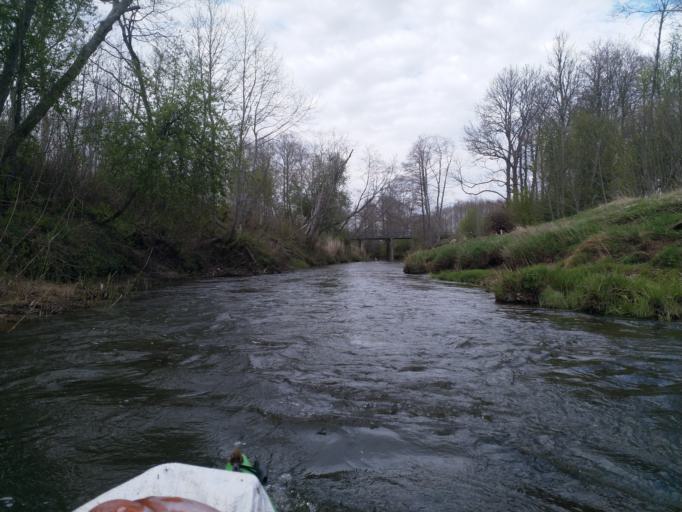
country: LV
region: Alsunga
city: Alsunga
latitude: 57.1248
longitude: 21.5496
